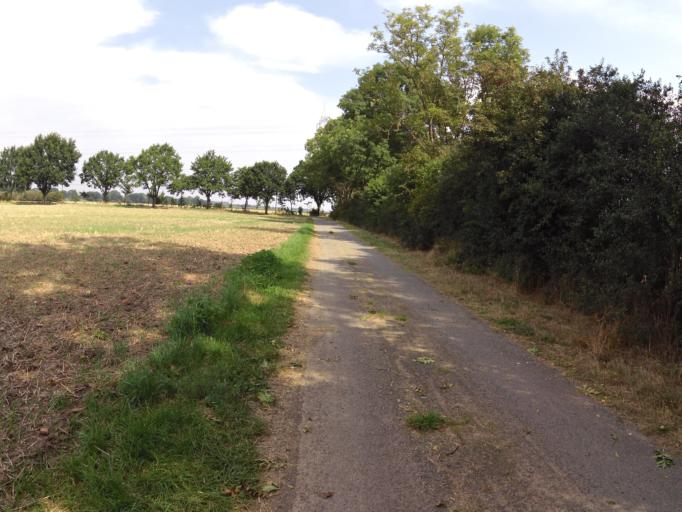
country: DE
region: Lower Saxony
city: Stolzenau
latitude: 52.5359
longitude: 9.0828
